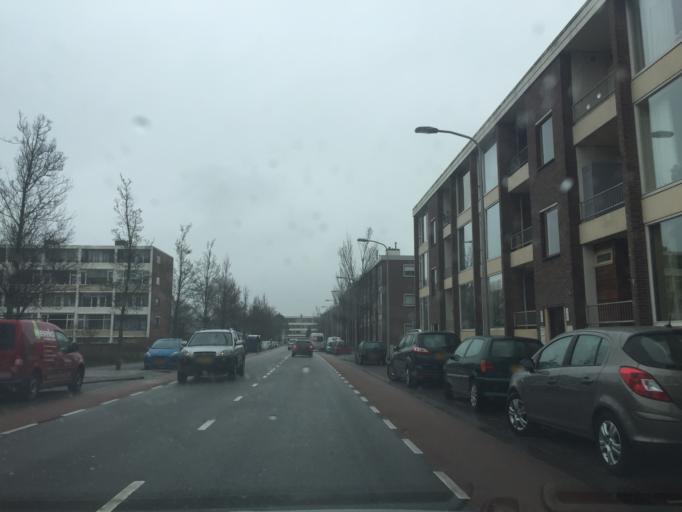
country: NL
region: South Holland
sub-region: Gemeente Katwijk
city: Katwijk aan Zee
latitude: 52.1982
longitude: 4.4084
